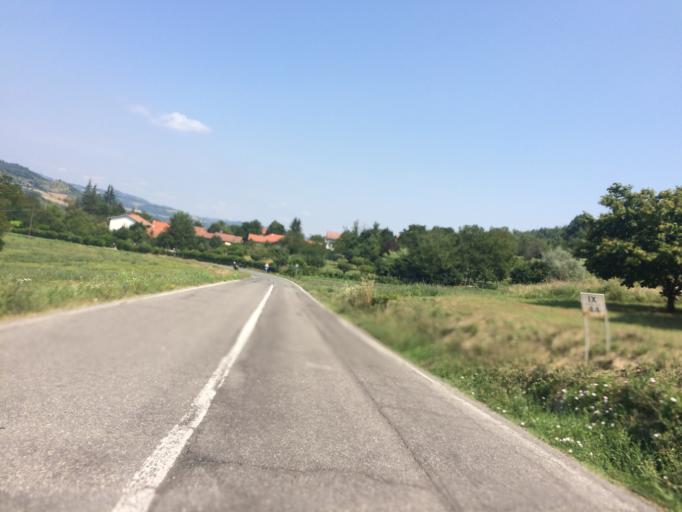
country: IT
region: Piedmont
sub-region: Provincia di Alessandria
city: Castelletto d'Erro
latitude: 44.6234
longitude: 8.4163
